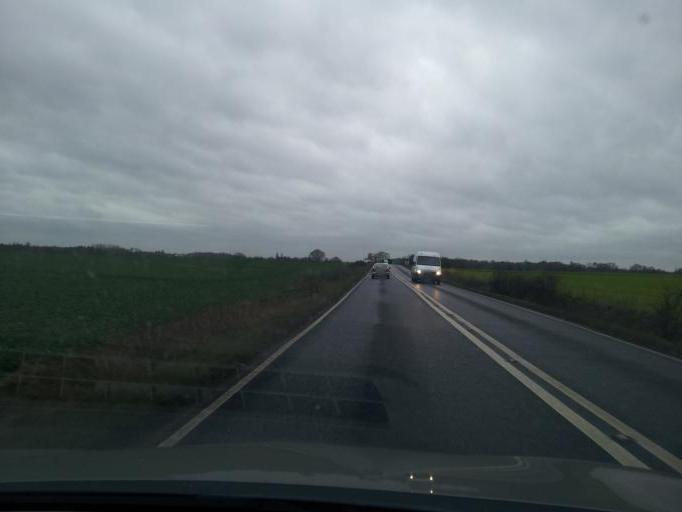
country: GB
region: England
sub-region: Suffolk
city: Thurston
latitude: 52.2781
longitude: 0.8003
